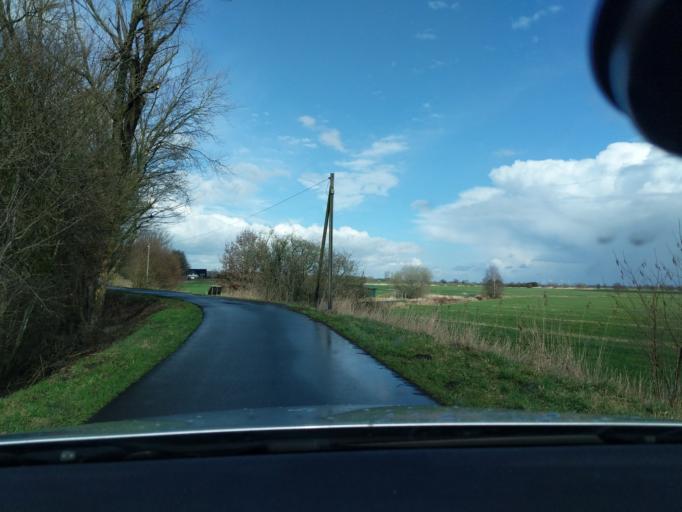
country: DE
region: Lower Saxony
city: Kranenburg
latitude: 53.6132
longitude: 9.2031
